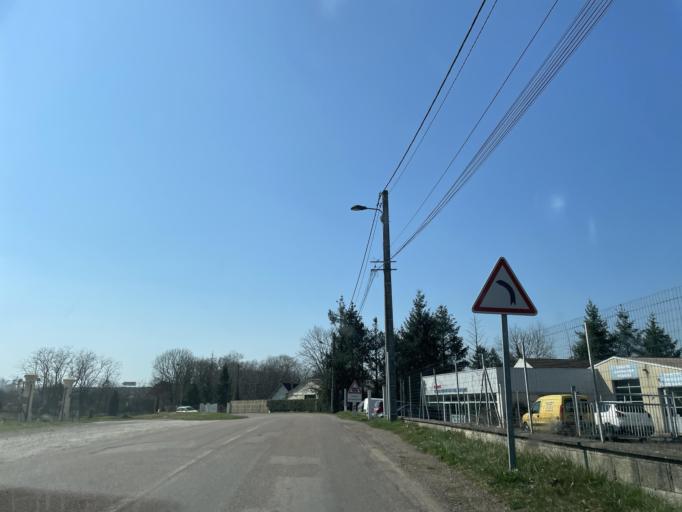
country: FR
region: Bourgogne
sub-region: Departement de la Cote-d'Or
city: Semur-en-Auxois
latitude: 47.4885
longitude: 4.3411
